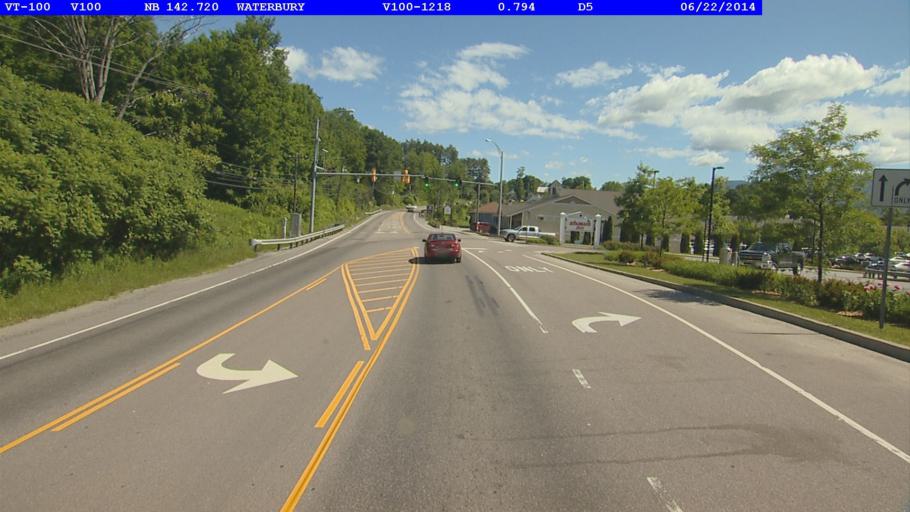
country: US
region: Vermont
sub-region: Washington County
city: Waterbury
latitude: 44.3463
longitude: -72.7458
